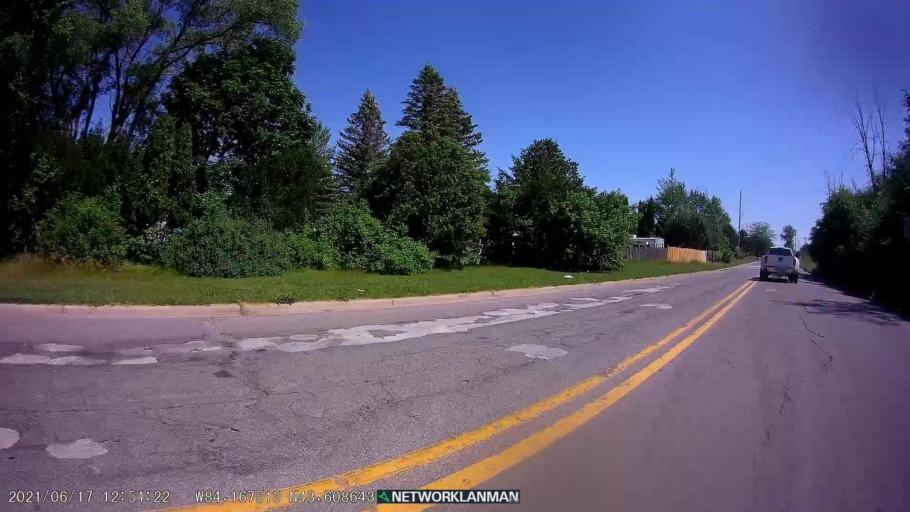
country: US
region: Michigan
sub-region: Midland County
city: Midland
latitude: 43.6078
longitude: -84.1674
